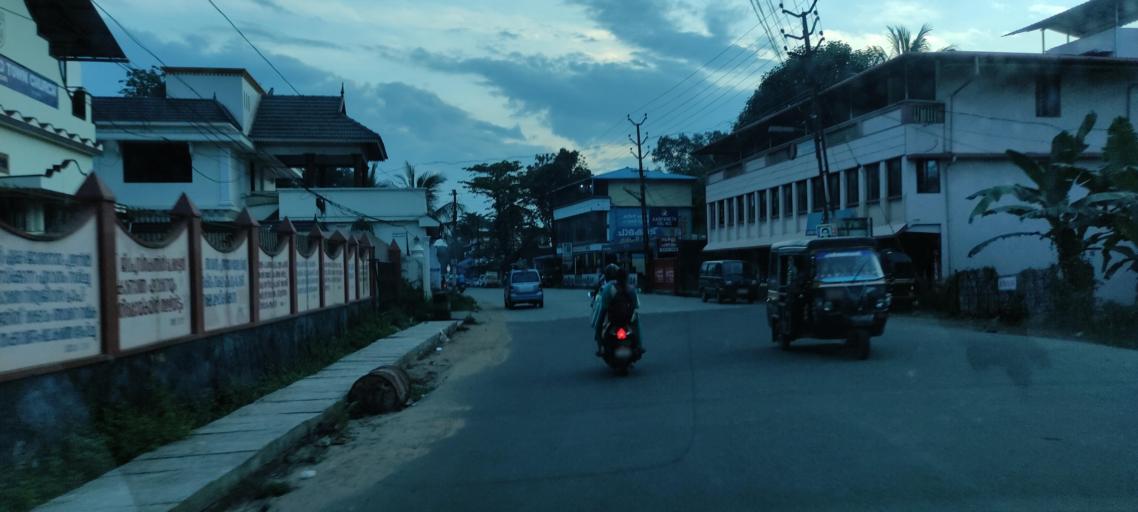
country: IN
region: Kerala
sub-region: Pattanamtitta
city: Adur
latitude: 9.1503
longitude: 76.7340
